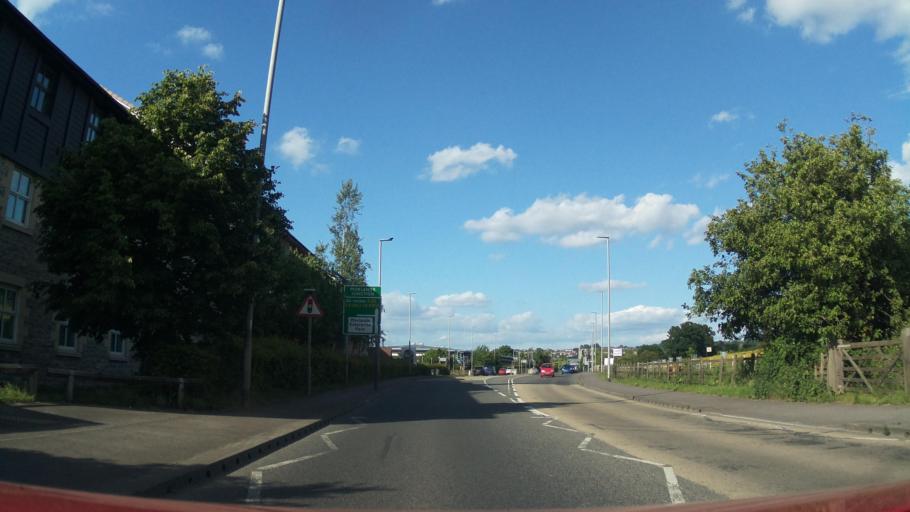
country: GB
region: England
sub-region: Somerset
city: Street
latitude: 51.1398
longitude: -2.7350
